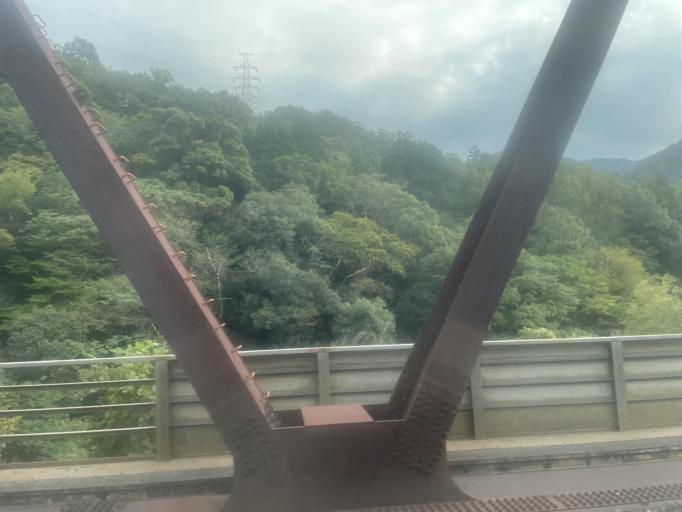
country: JP
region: Hyogo
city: Takarazuka
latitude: 34.8173
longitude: 135.3197
